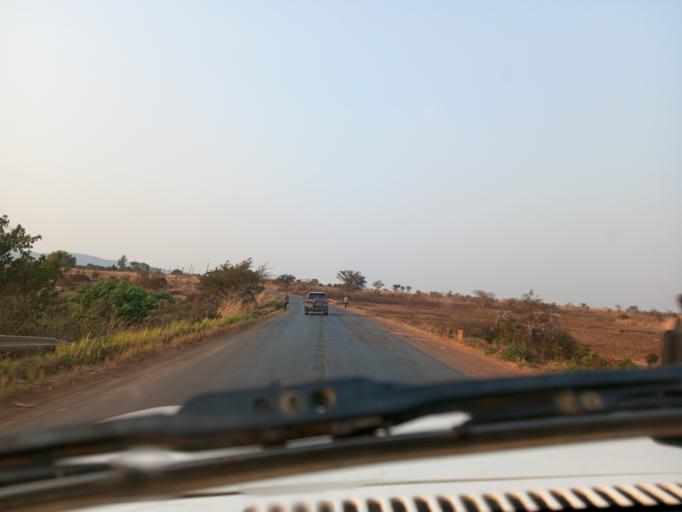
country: ZM
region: Northern
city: Mpika
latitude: -11.9006
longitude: 31.4138
